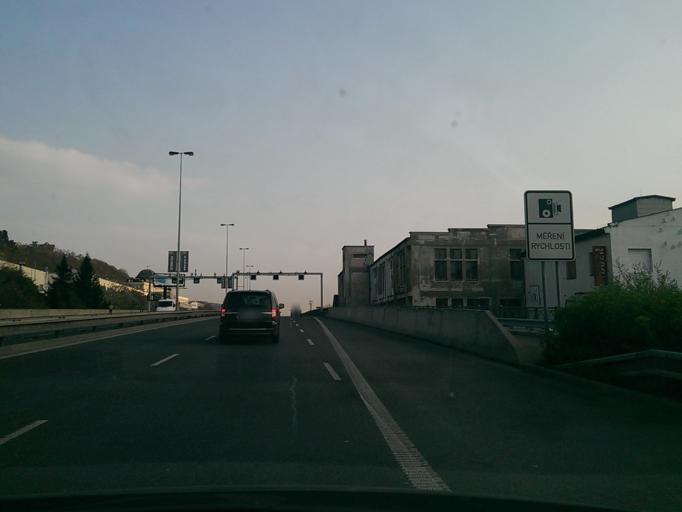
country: CZ
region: Praha
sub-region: Praha 2
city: Vysehrad
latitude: 50.0523
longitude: 14.4080
